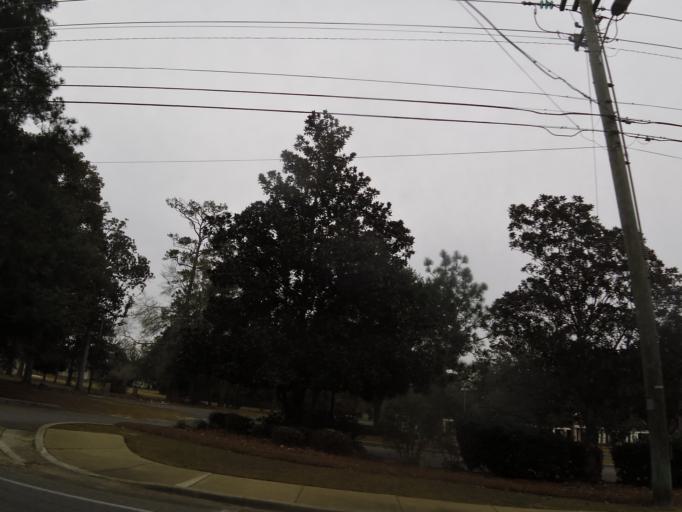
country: US
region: Georgia
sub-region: Thomas County
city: Thomasville
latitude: 30.8268
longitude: -83.9703
